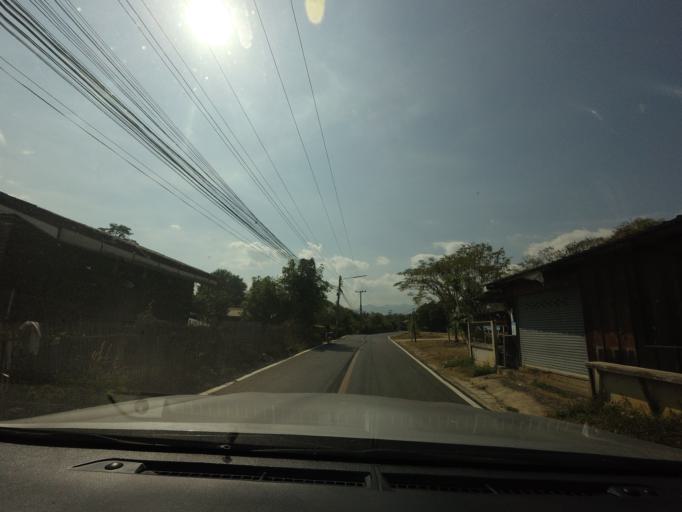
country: TH
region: Mae Hong Son
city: Wiang Nuea
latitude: 19.3842
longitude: 98.4390
